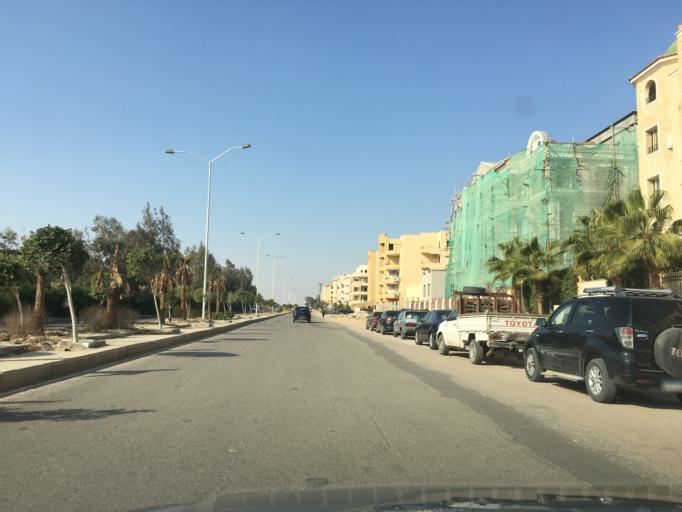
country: EG
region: Al Jizah
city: Madinat Sittah Uktubar
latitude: 29.9969
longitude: 30.9774
